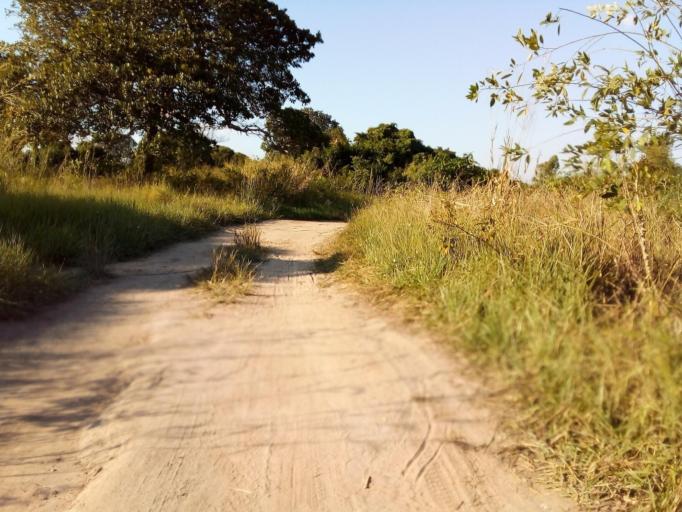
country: MZ
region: Zambezia
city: Quelimane
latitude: -17.5544
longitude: 36.6988
